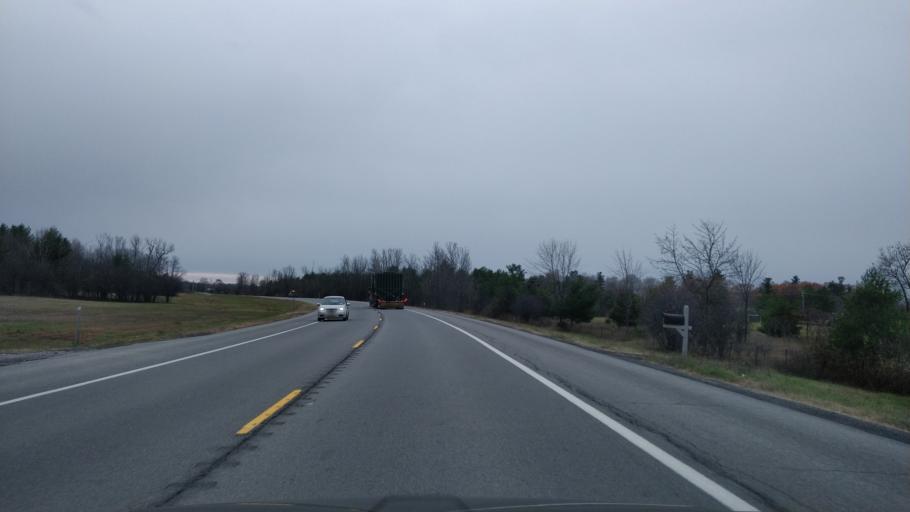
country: CA
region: Ontario
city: Brockville
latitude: 44.5896
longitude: -75.6406
